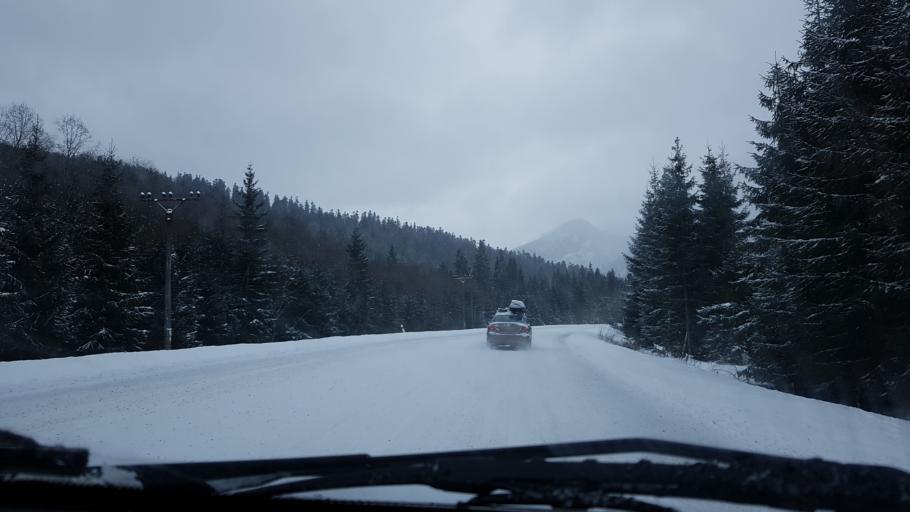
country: PL
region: Lesser Poland Voivodeship
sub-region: Powiat tatrzanski
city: Bukowina Tatrzanska
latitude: 49.2895
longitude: 20.1734
